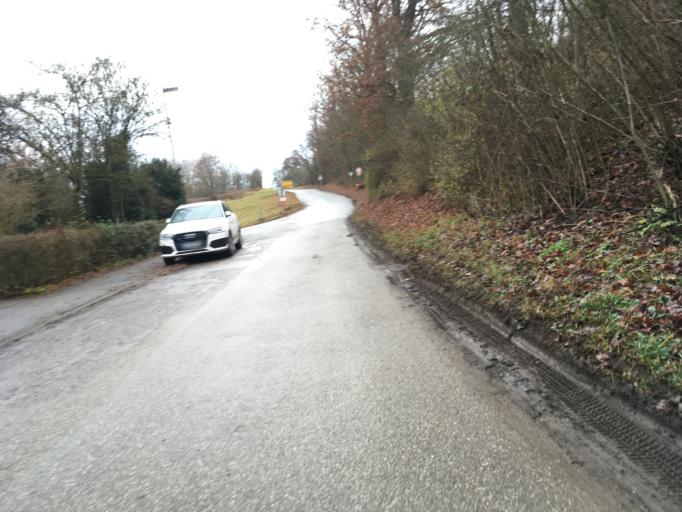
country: DE
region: Baden-Wuerttemberg
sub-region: Regierungsbezirk Stuttgart
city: Talheim
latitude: 49.0762
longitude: 9.1999
